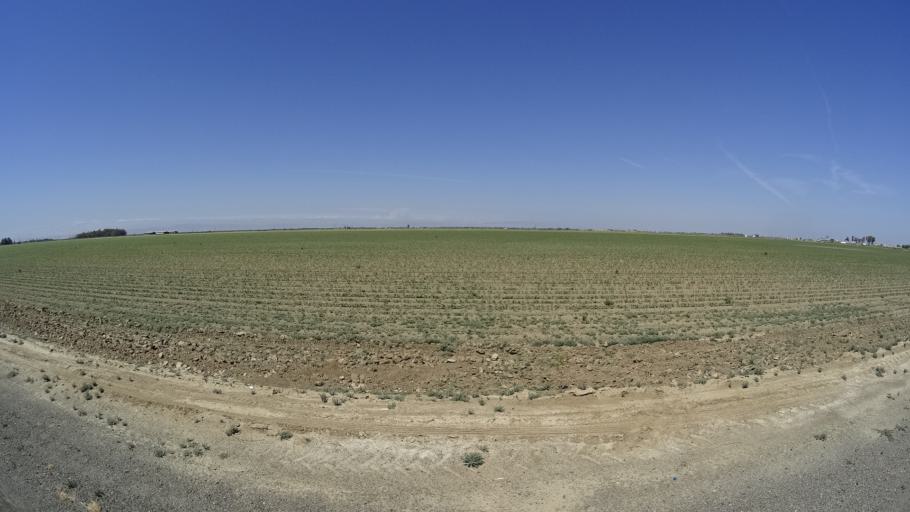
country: US
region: California
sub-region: Kings County
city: Lemoore
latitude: 36.2610
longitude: -119.7990
